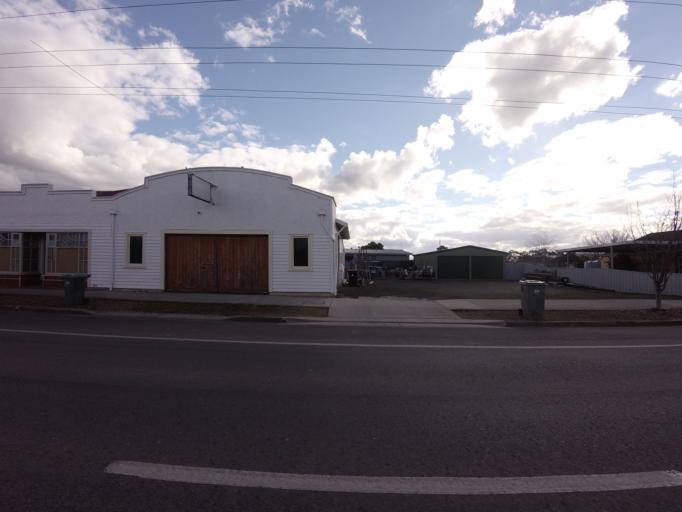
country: AU
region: Tasmania
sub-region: Northern Midlands
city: Longford
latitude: -41.6845
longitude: 147.0806
